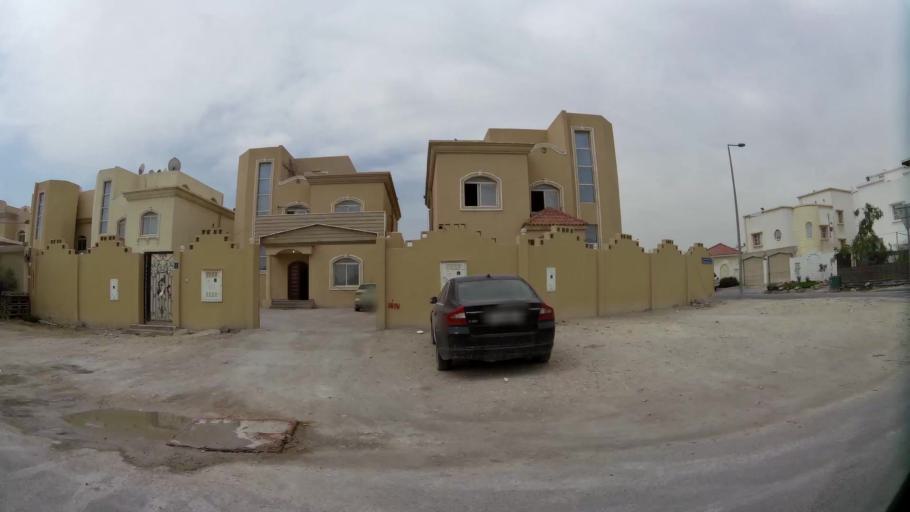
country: QA
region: Baladiyat ad Dawhah
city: Doha
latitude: 25.2207
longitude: 51.4738
